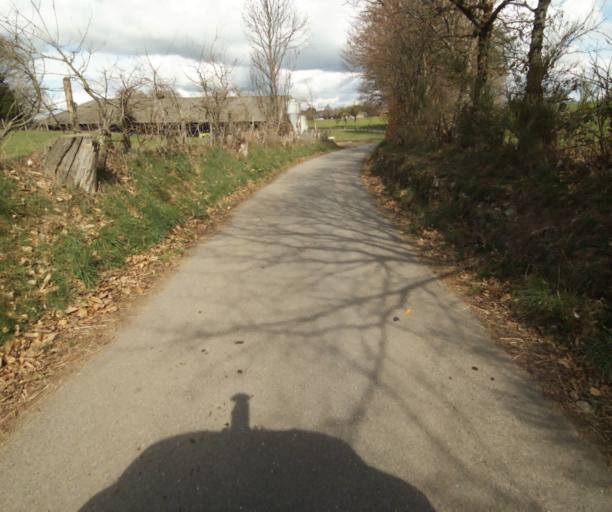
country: FR
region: Limousin
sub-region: Departement de la Correze
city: Correze
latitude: 45.3644
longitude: 1.8977
